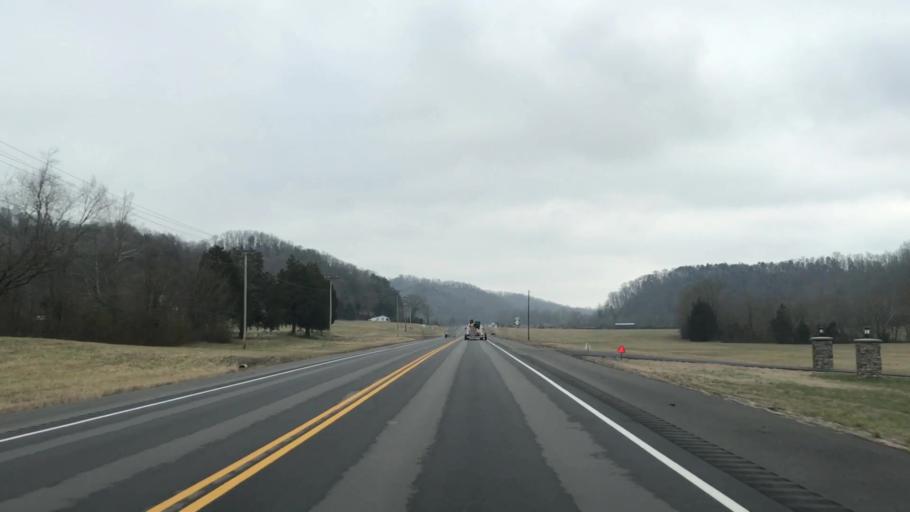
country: US
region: Kentucky
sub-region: Cumberland County
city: Burkesville
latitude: 36.8407
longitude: -85.3704
